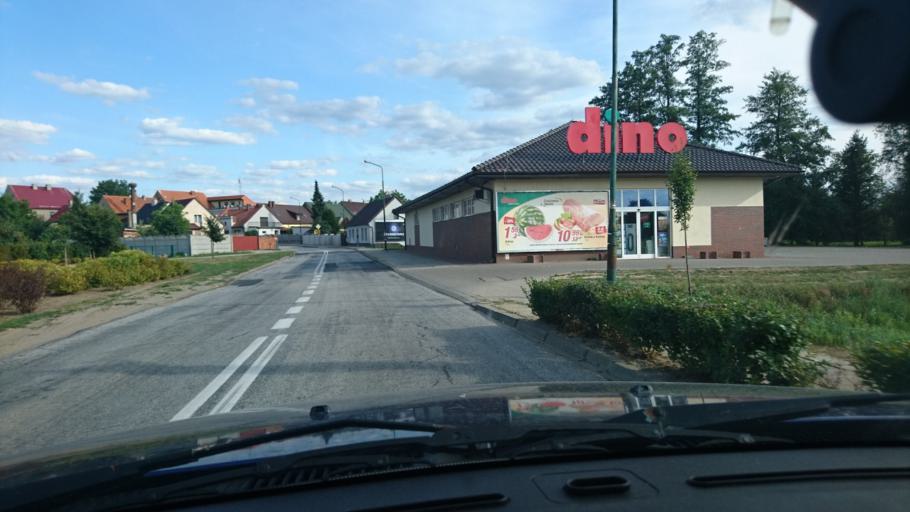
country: PL
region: Greater Poland Voivodeship
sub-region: Powiat krotoszynski
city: Sulmierzyce
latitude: 51.6073
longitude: 17.5249
